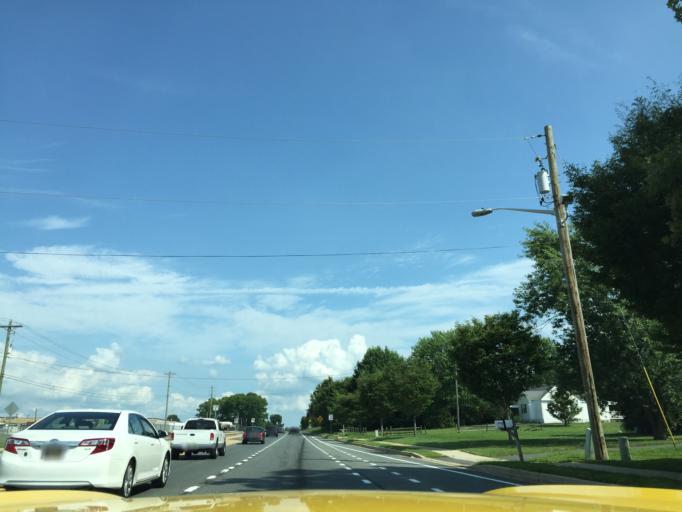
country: US
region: Delaware
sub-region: New Castle County
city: Newport
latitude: 39.6761
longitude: -75.6252
